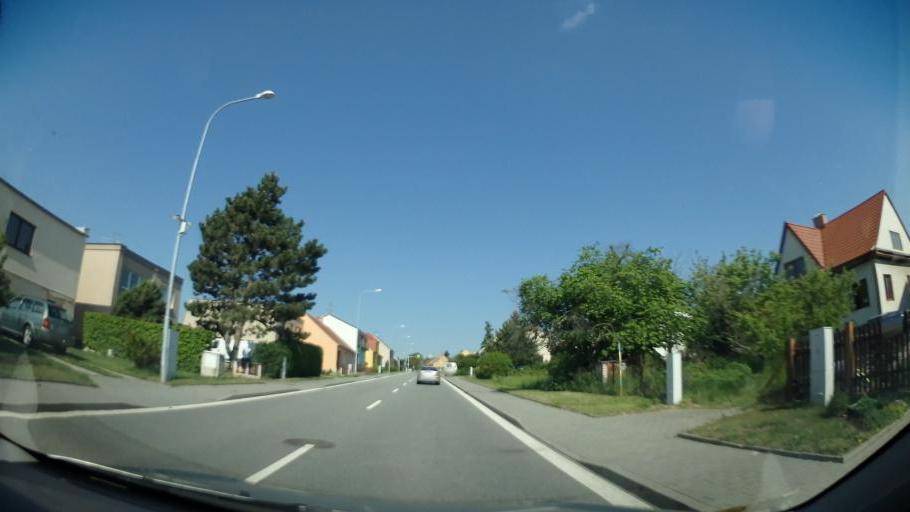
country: CZ
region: South Moravian
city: Zbraslav
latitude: 49.1801
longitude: 16.2941
